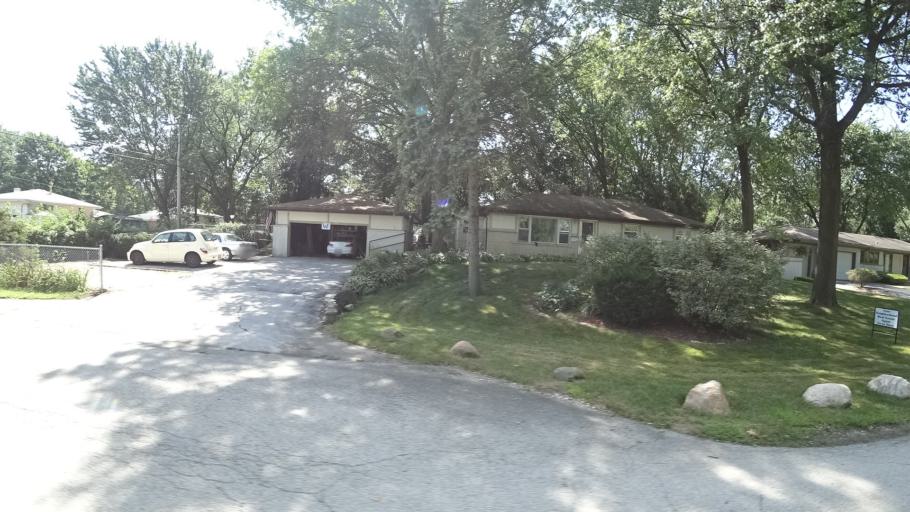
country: US
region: Illinois
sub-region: Cook County
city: Orland Park
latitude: 41.6284
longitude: -87.8445
